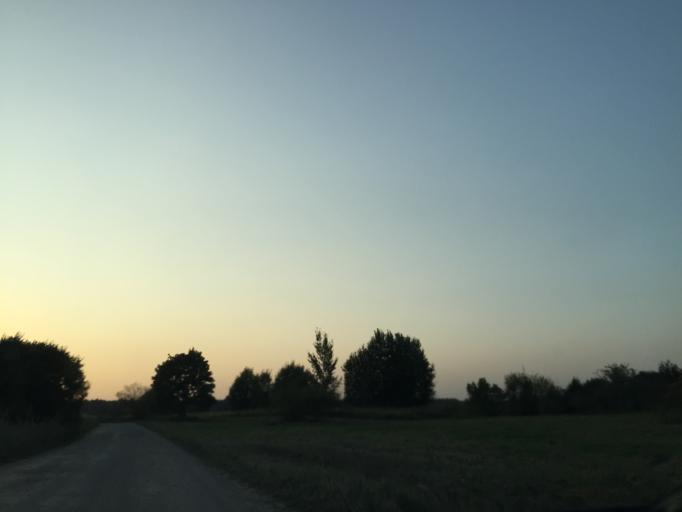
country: LV
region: Lielvarde
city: Lielvarde
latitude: 56.7614
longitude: 24.7785
